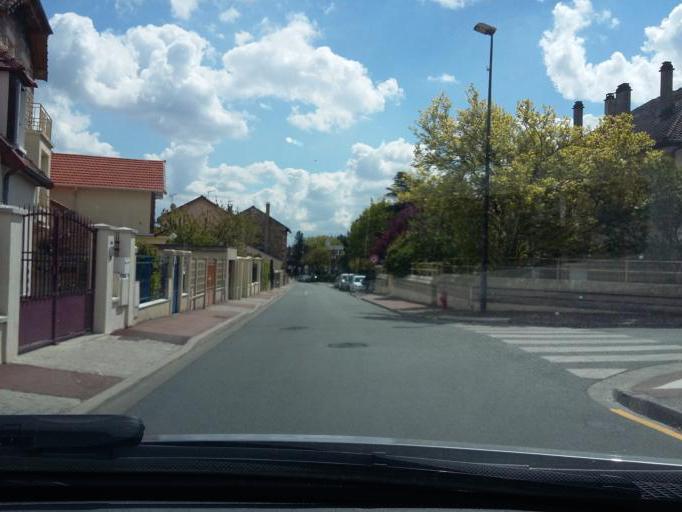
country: FR
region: Ile-de-France
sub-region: Departement du Val-d'Oise
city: Saint-Gratien
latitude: 48.9659
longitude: 2.2927
